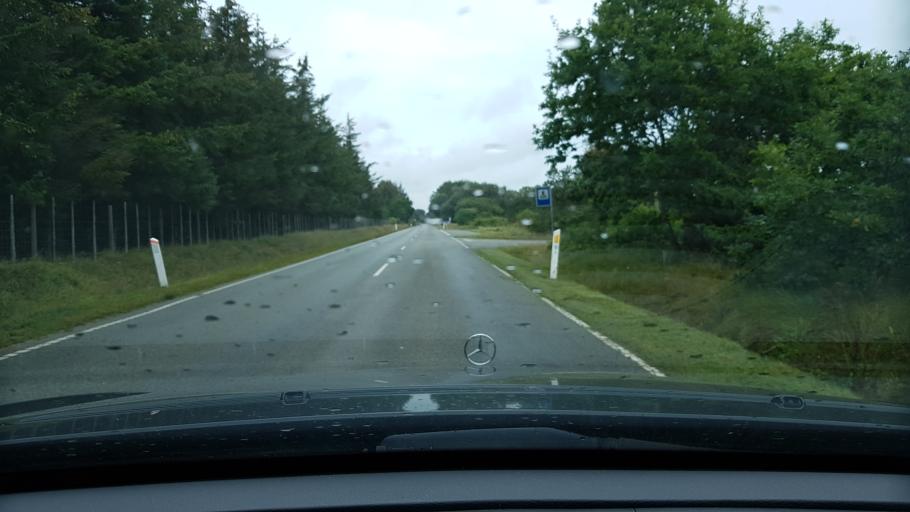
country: DK
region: North Denmark
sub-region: Alborg Kommune
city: Hals
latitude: 56.8290
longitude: 10.2686
